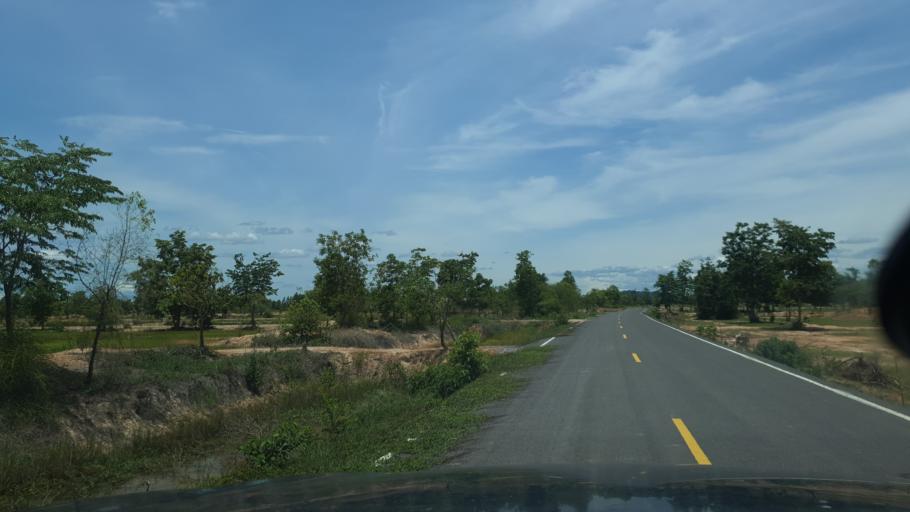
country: TH
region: Sukhothai
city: Ban Na
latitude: 17.1507
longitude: 99.6520
